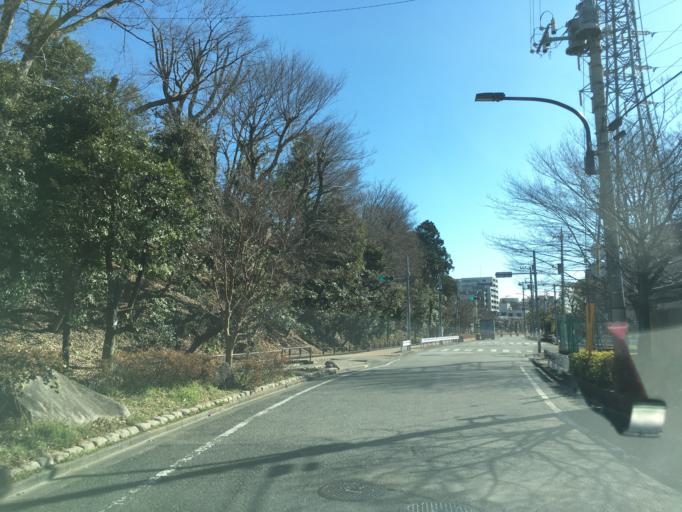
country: JP
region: Tokyo
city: Kokubunji
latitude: 35.6715
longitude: 139.4537
